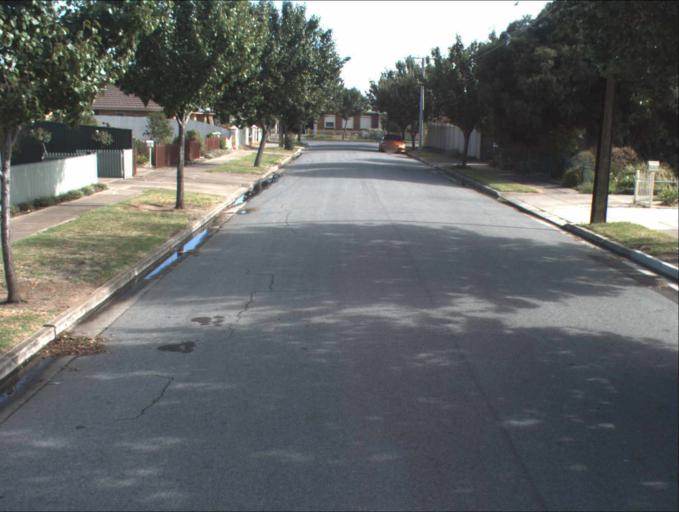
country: AU
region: South Australia
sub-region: Charles Sturt
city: Woodville North
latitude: -34.8652
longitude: 138.5635
